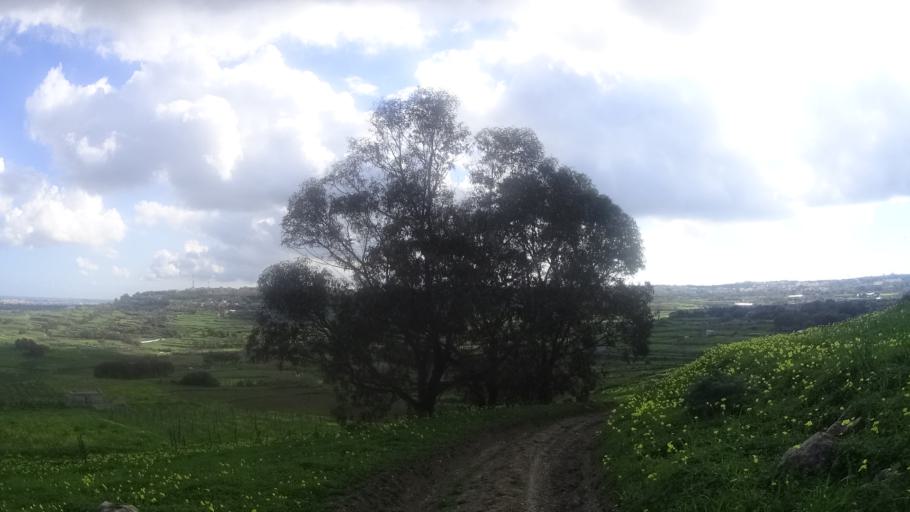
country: MT
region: L-Imtarfa
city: Imtarfa
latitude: 35.8992
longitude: 14.3860
